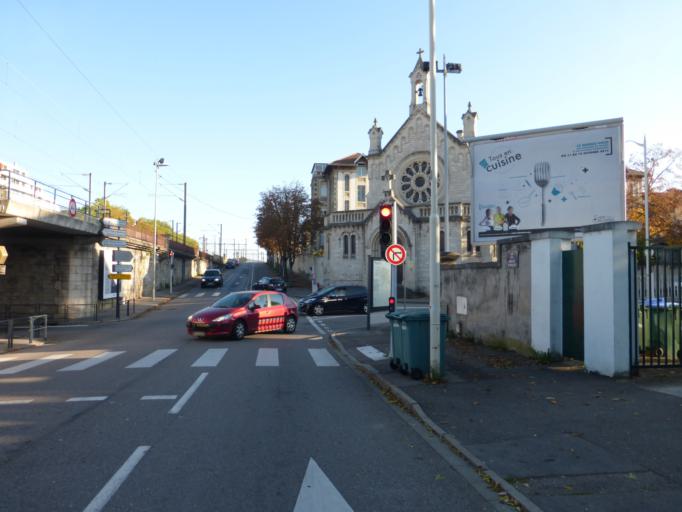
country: FR
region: Lorraine
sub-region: Departement de Meurthe-et-Moselle
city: Nancy
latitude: 48.6795
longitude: 6.1891
